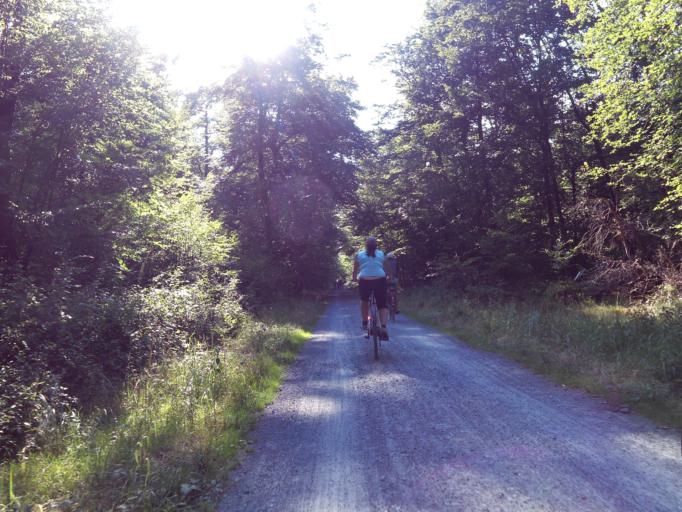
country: DE
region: Hesse
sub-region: Regierungsbezirk Darmstadt
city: Nauheim
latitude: 49.9750
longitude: 8.5002
